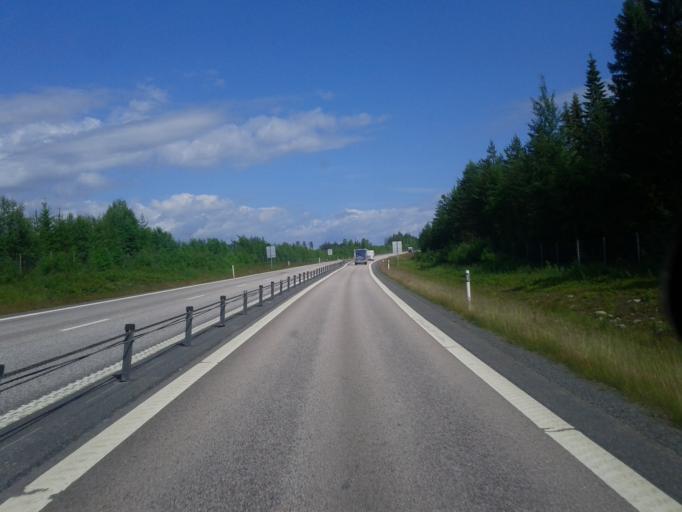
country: SE
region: Vaesternorrland
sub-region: OErnskoeldsviks Kommun
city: Husum
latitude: 63.4419
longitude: 19.2145
